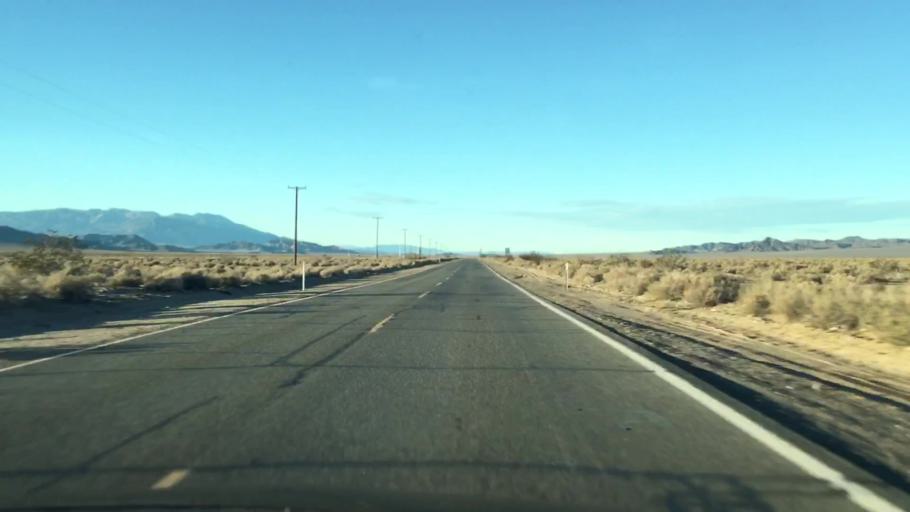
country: US
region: California
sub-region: San Bernardino County
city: Fort Irwin
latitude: 35.2806
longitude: -116.0766
